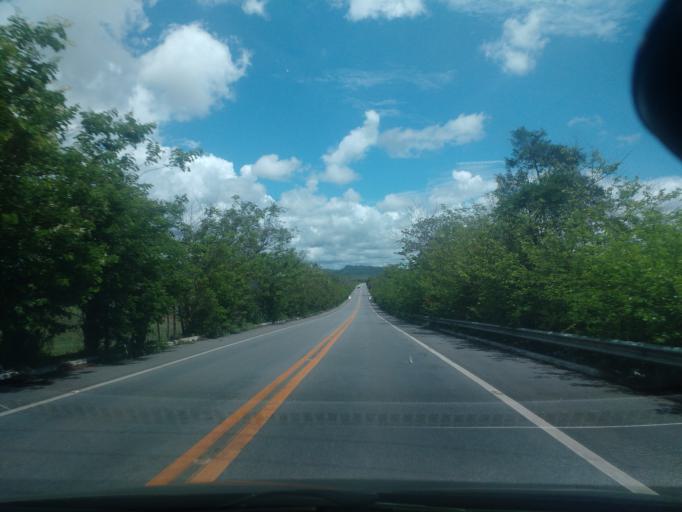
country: BR
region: Alagoas
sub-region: Uniao Dos Palmares
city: Uniao dos Palmares
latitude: -9.1371
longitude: -36.0202
